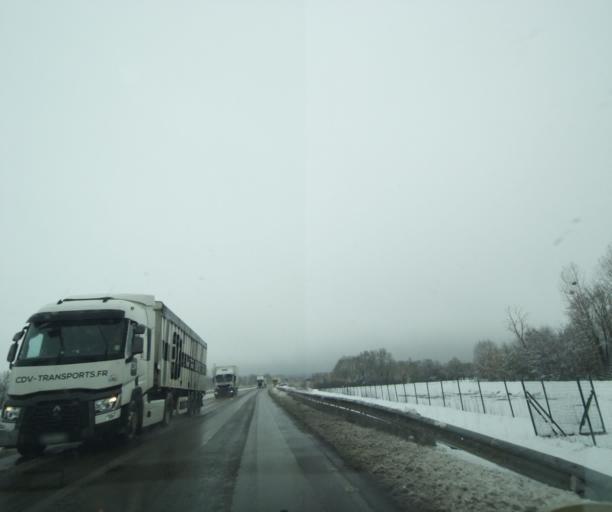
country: FR
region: Champagne-Ardenne
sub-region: Departement de la Haute-Marne
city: Saint-Dizier
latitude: 48.5810
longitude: 4.8862
